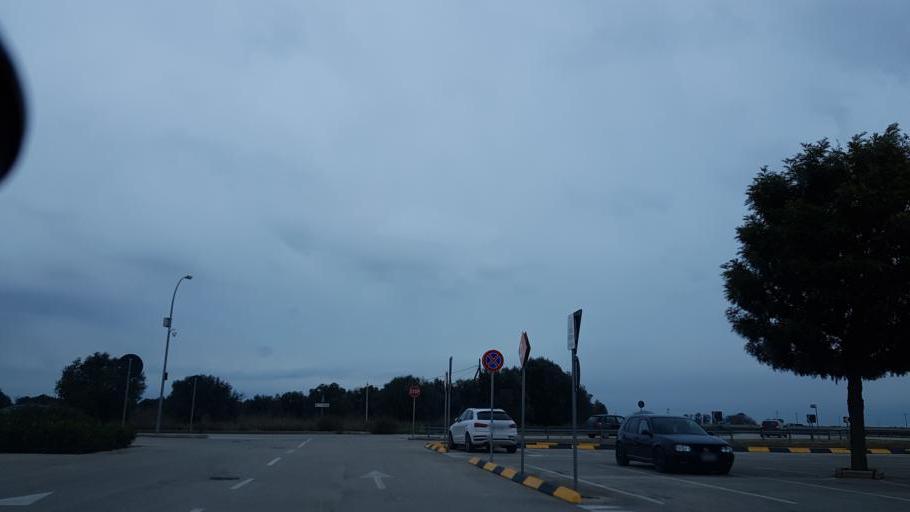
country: IT
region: Apulia
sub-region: Provincia di Brindisi
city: Mesagne
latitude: 40.5794
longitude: 17.8387
